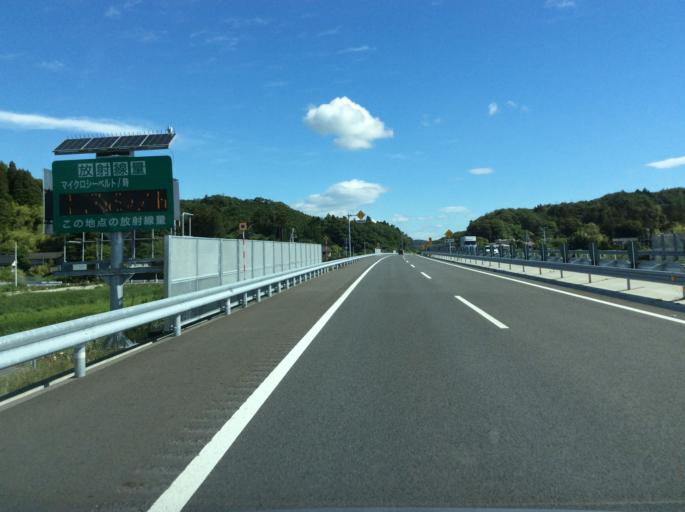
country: JP
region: Fukushima
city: Namie
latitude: 37.4114
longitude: 140.9621
